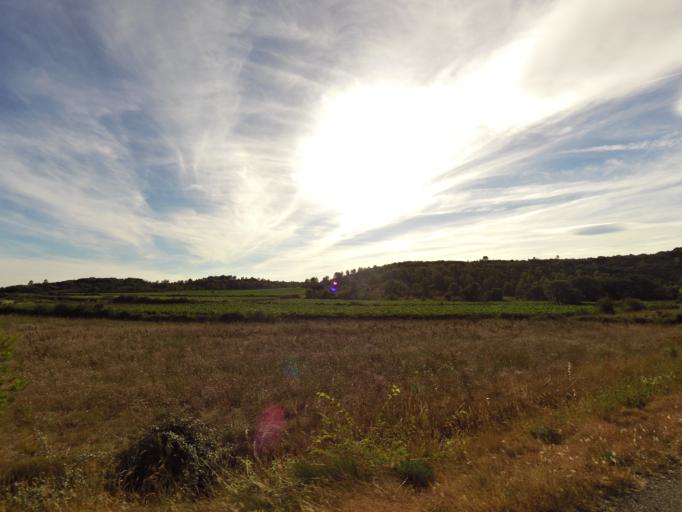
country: FR
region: Languedoc-Roussillon
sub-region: Departement du Gard
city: Congenies
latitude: 43.8091
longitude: 4.1496
